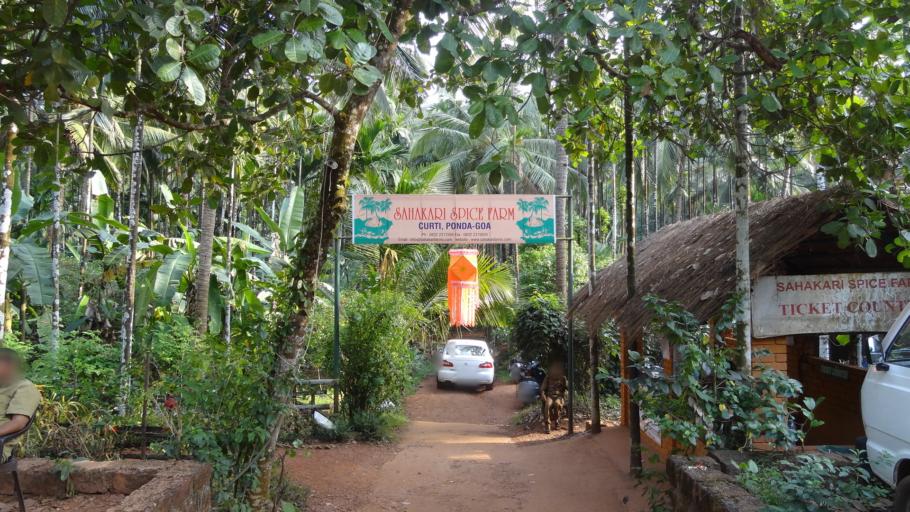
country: IN
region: Goa
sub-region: North Goa
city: Ponda
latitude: 15.4087
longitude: 74.0244
